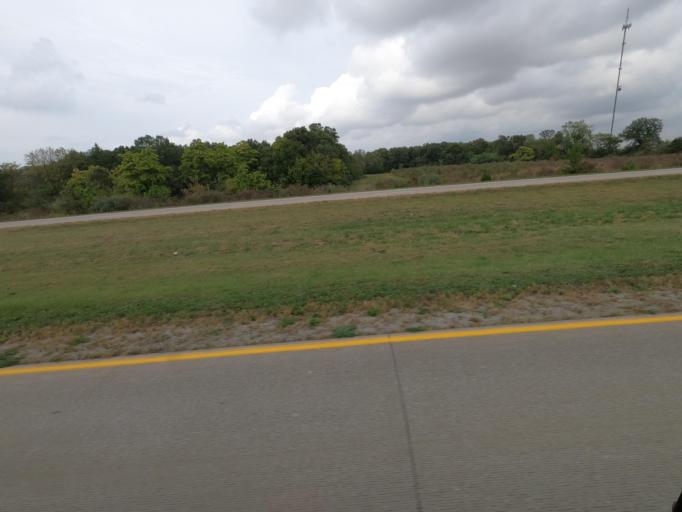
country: US
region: Iowa
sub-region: Wapello County
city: Ottumwa
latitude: 40.9984
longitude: -92.3270
